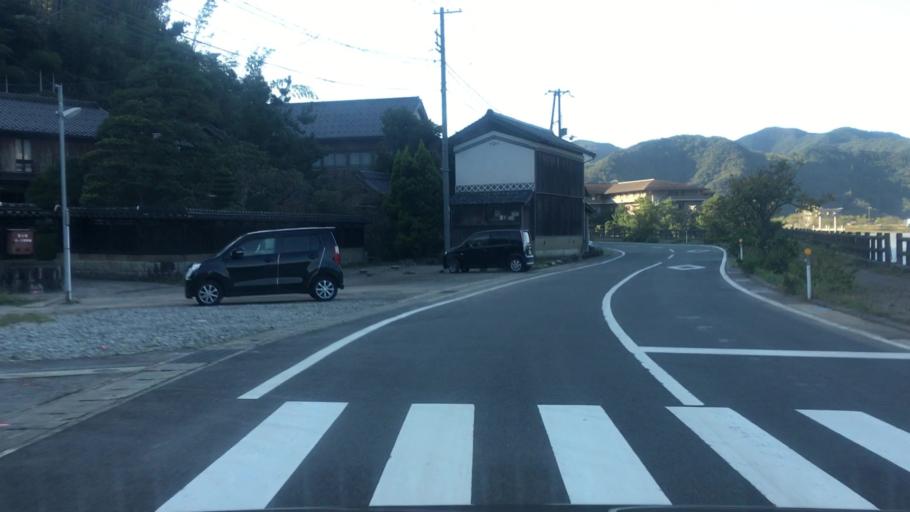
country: JP
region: Hyogo
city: Toyooka
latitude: 35.6184
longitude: 134.8216
